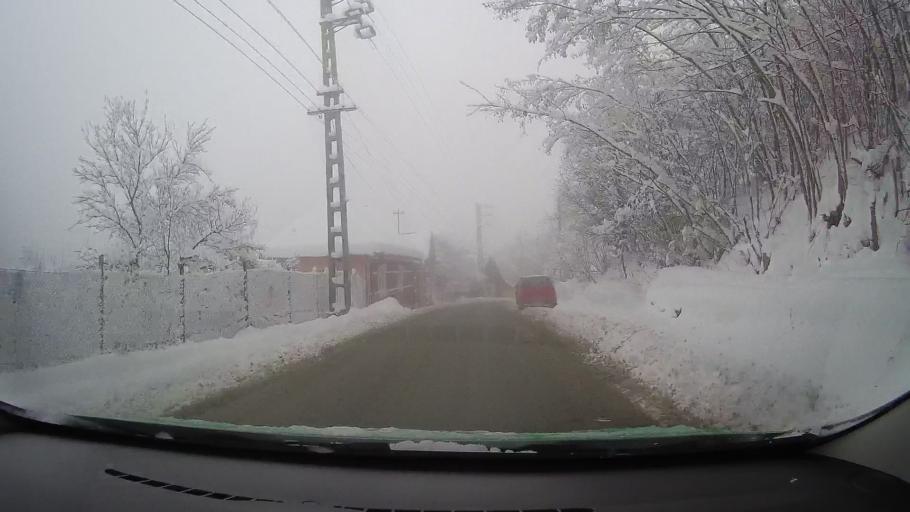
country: RO
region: Sibiu
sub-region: Comuna Poiana Sibiului
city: Poiana Sibiului
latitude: 45.8037
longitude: 23.7752
